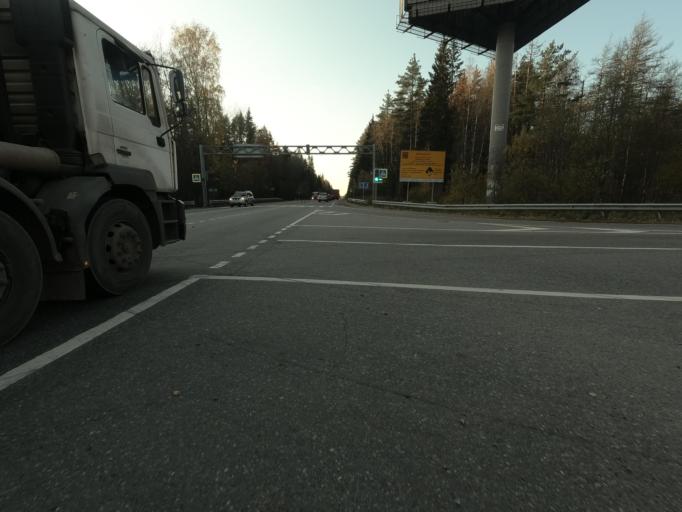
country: RU
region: St.-Petersburg
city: Pesochnyy
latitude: 60.1822
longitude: 30.1295
